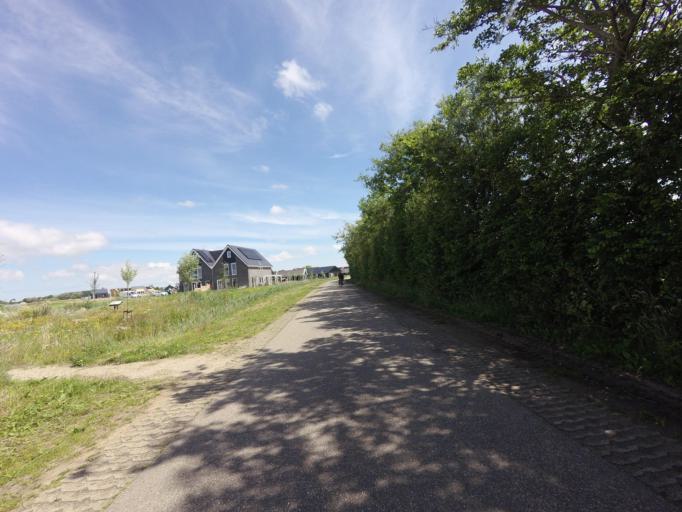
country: NL
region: North Holland
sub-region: Gemeente Texel
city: Den Burg
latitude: 53.0565
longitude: 4.8113
